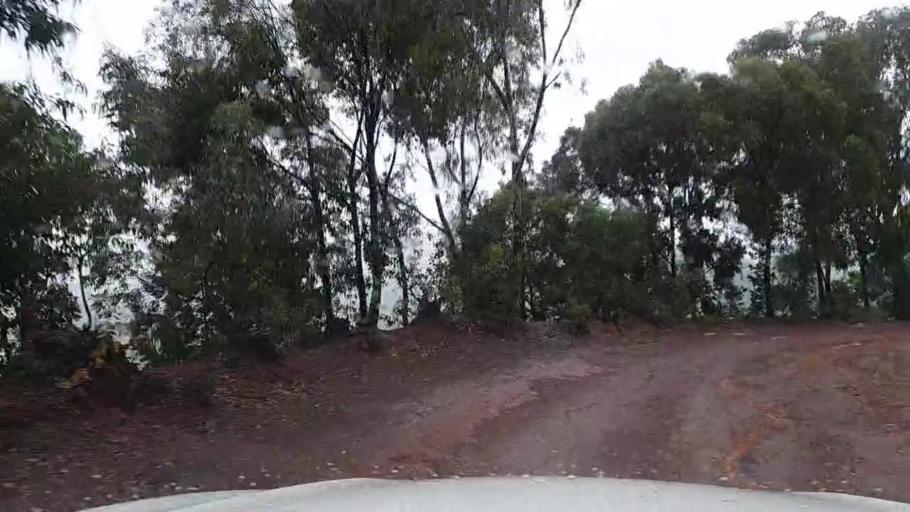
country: RW
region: Kigali
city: Kigali
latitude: -1.7650
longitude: 29.9928
